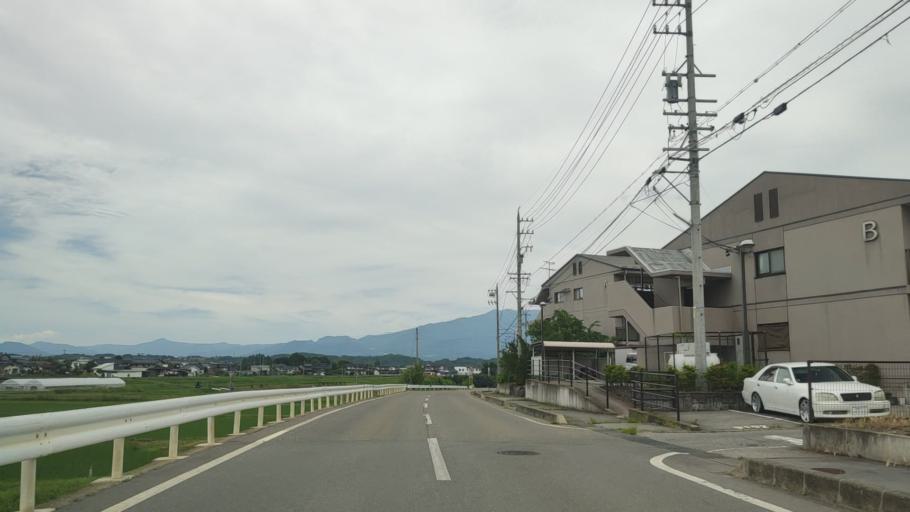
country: JP
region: Nagano
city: Kamimaruko
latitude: 36.2941
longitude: 138.3173
